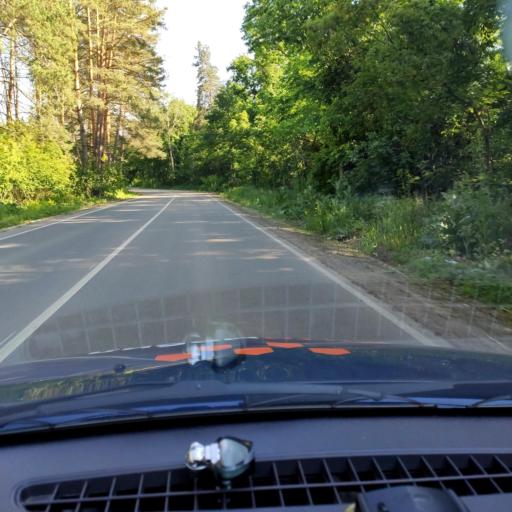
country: RU
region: Voronezj
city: Podgornoye
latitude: 51.8300
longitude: 39.1431
